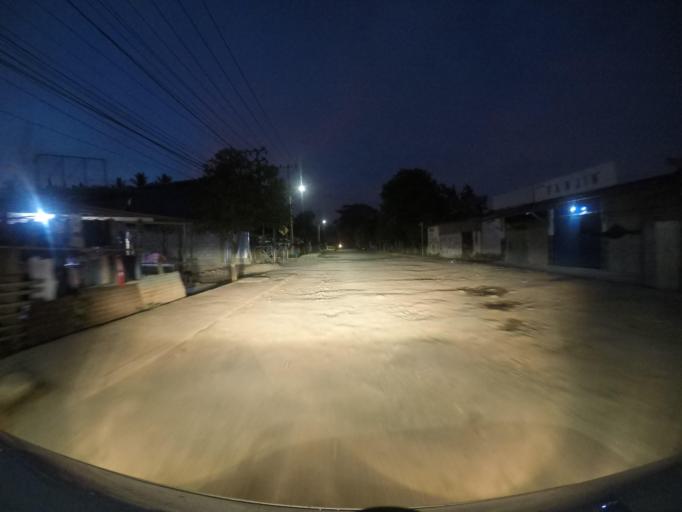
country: TL
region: Viqueque
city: Viqueque
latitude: -8.8587
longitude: 126.3652
